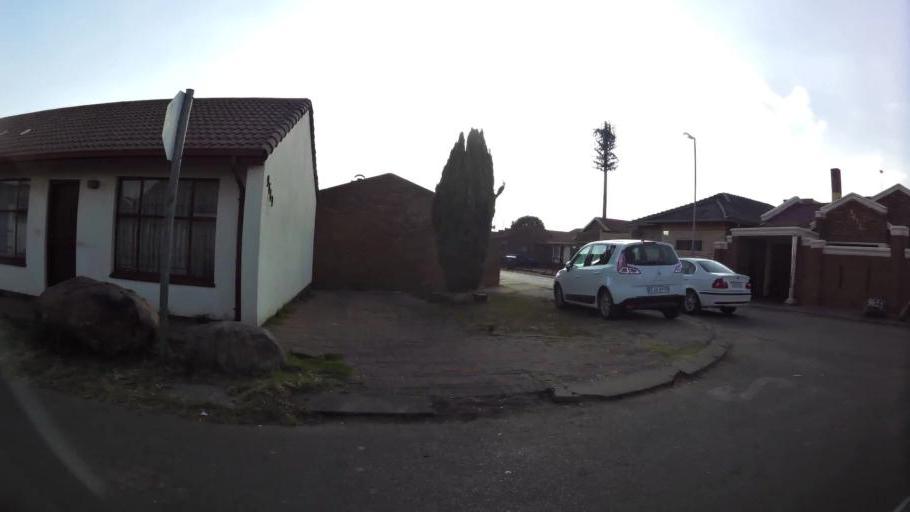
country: ZA
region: Gauteng
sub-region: City of Johannesburg Metropolitan Municipality
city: Soweto
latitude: -26.2696
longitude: 27.9153
